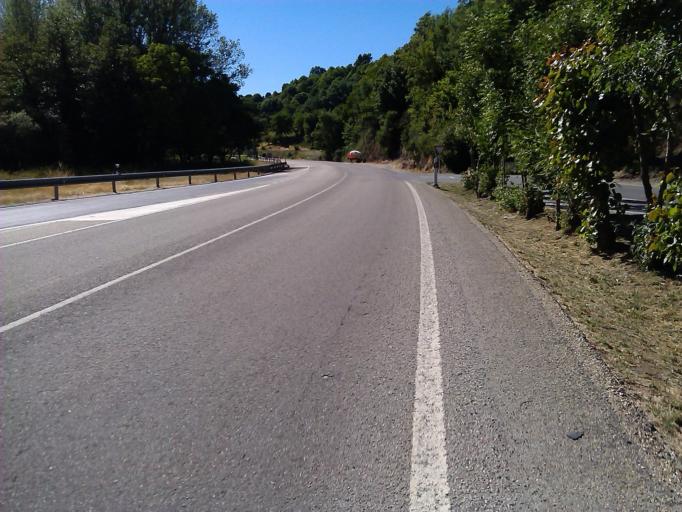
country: ES
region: Castille and Leon
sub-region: Provincia de Leon
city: Vega de Valcarce
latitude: 42.6597
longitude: -6.9159
